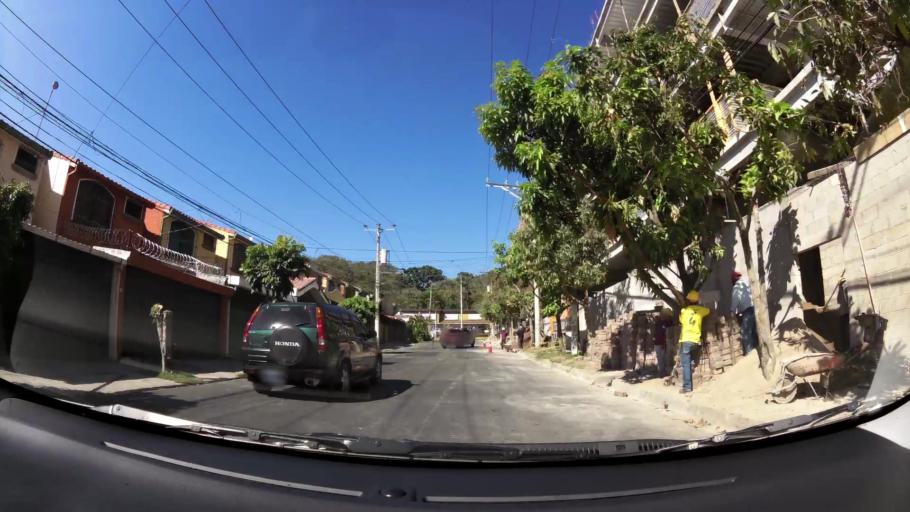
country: SV
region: La Libertad
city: Santa Tecla
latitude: 13.6771
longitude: -89.2762
